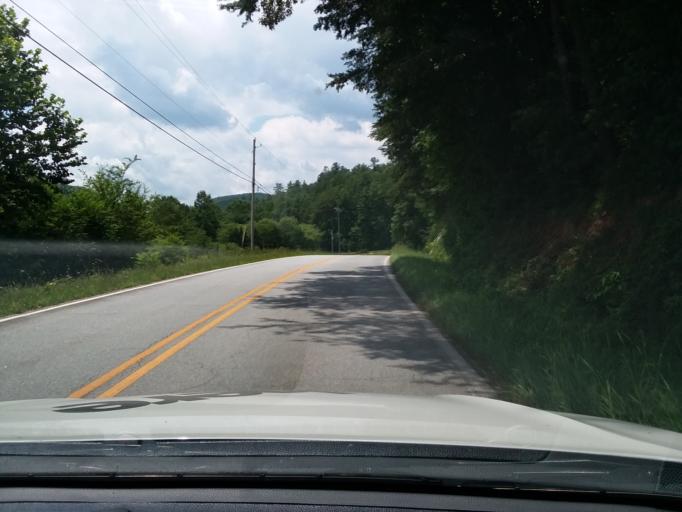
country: US
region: Georgia
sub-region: Rabun County
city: Mountain City
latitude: 34.8869
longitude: -83.3313
